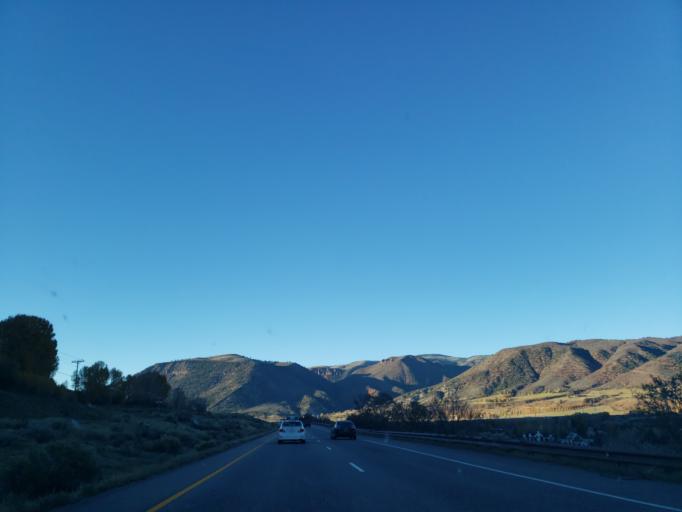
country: US
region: Colorado
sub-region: Pitkin County
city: Snowmass Village
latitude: 39.2689
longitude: -106.8904
